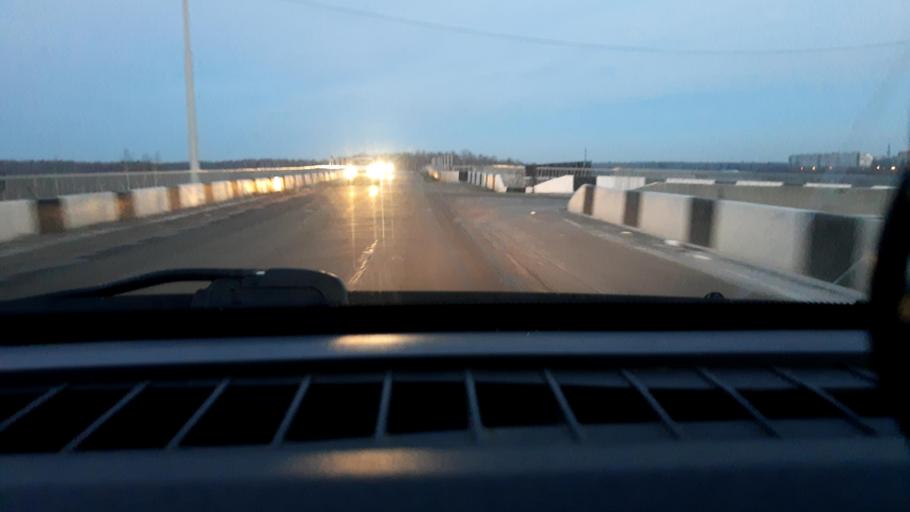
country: RU
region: Nizjnij Novgorod
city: Gorbatovka
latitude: 56.2808
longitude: 43.8423
